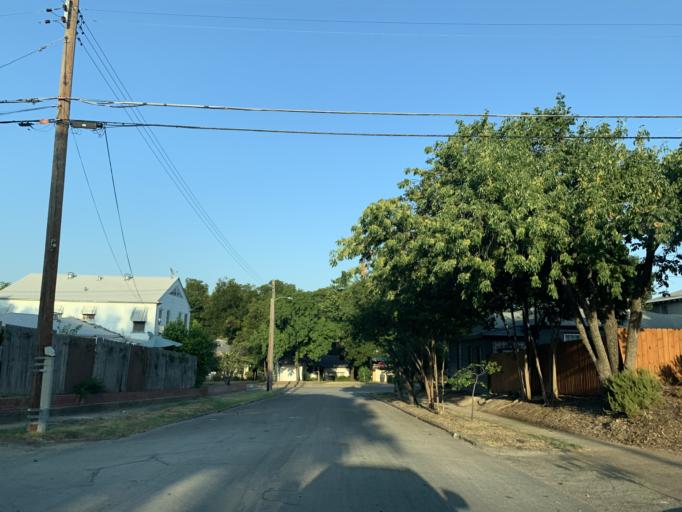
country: US
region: Texas
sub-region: Dallas County
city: Cockrell Hill
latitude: 32.7485
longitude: -96.8545
